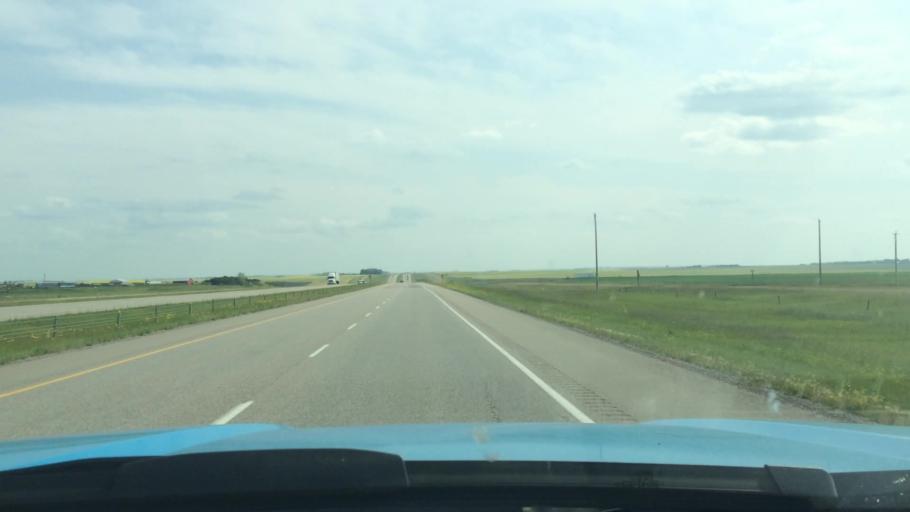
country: CA
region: Alberta
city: Carstairs
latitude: 51.6070
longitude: -114.0256
